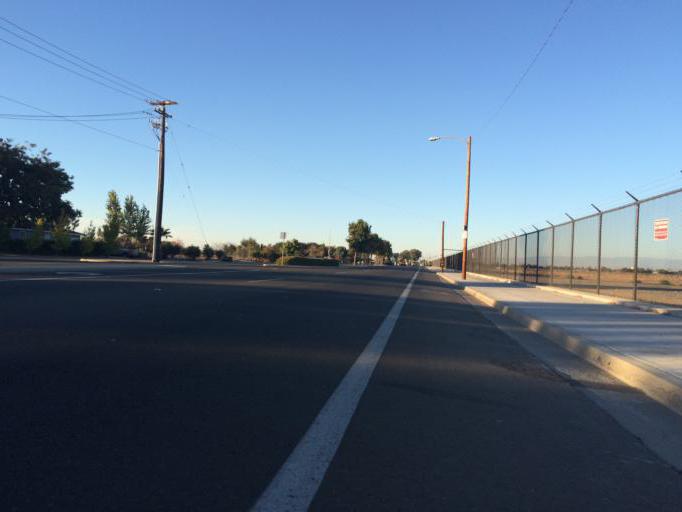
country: US
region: California
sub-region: Fresno County
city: Tarpey Village
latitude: 36.7828
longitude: -119.7364
